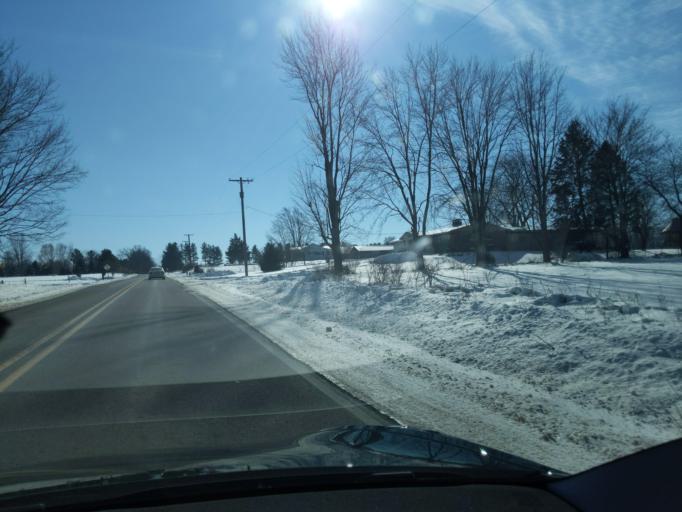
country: US
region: Michigan
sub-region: Livingston County
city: Fowlerville
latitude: 42.5444
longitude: -84.0685
